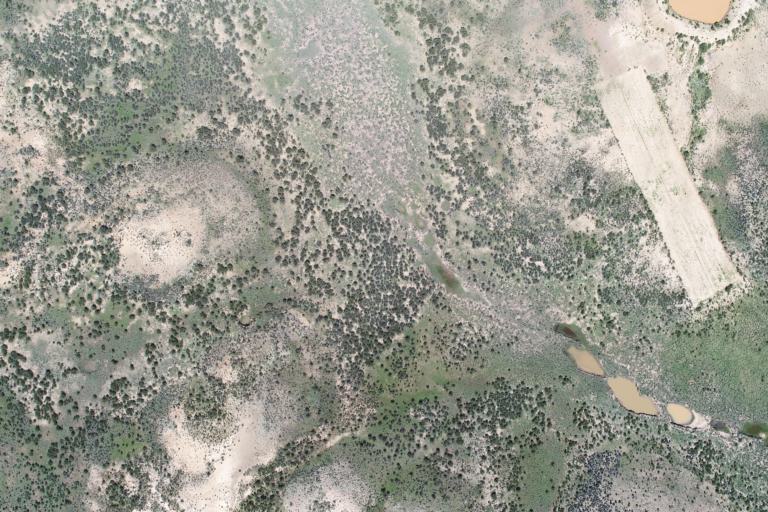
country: BO
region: La Paz
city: Curahuara de Carangas
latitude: -17.2938
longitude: -68.5157
